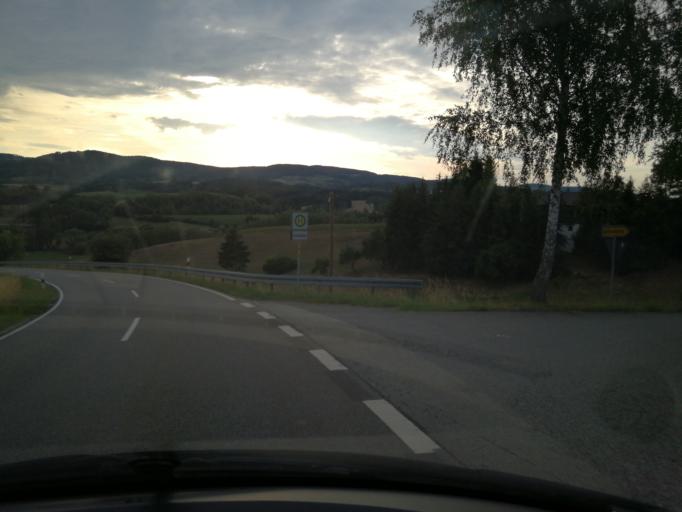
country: DE
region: Bavaria
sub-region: Lower Bavaria
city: Rattiszell
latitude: 49.0359
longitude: 12.6626
